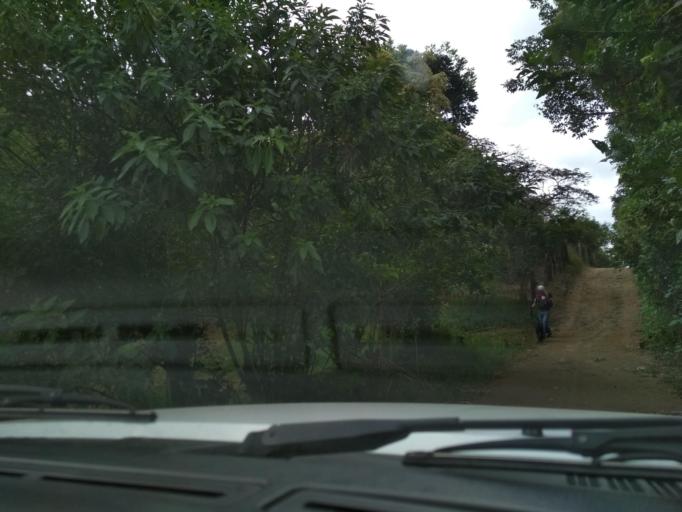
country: MX
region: Veracruz
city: El Castillo
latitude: 19.5784
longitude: -96.8593
